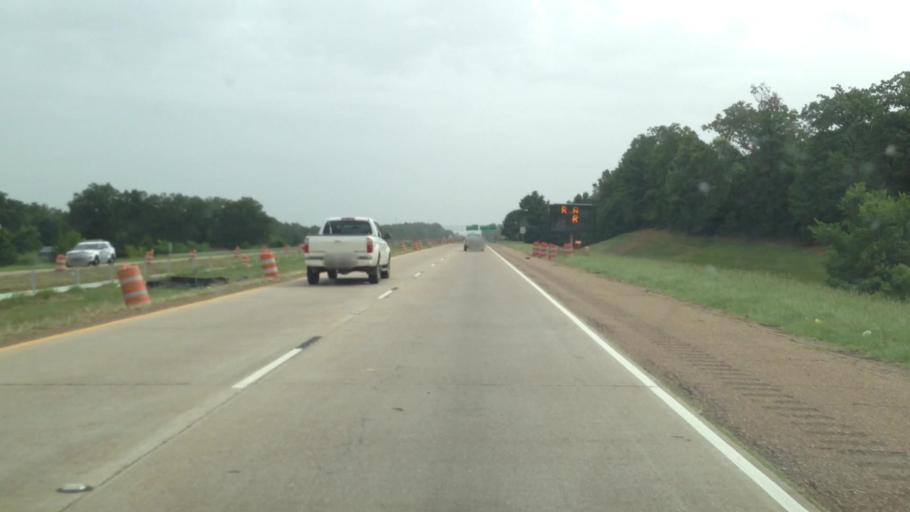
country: US
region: Louisiana
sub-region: Caddo Parish
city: Shreveport
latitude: 32.4671
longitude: -93.8416
